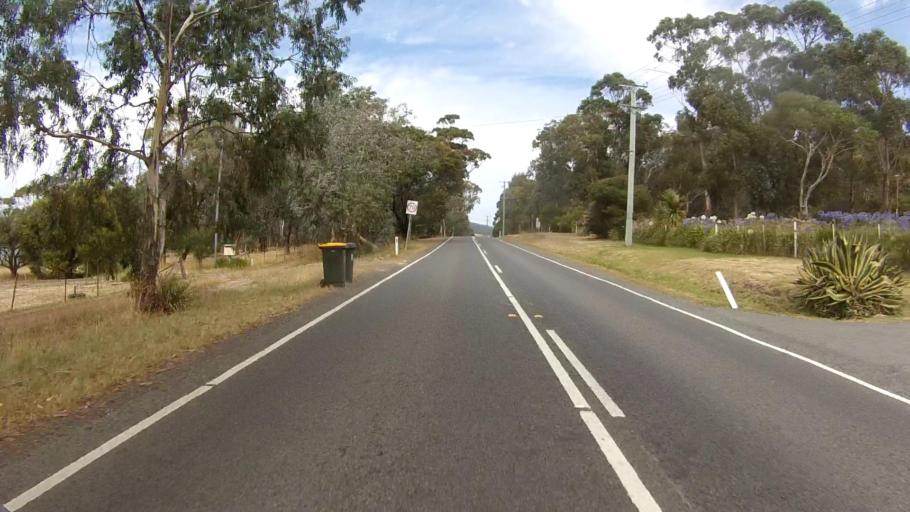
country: AU
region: Tasmania
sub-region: Clarence
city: Lauderdale
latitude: -42.8970
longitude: 147.4807
